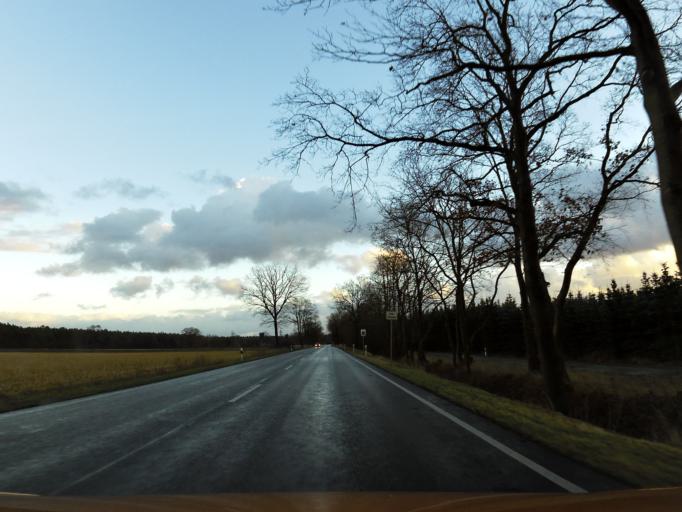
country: DE
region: Lower Saxony
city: Meinersen
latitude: 52.4580
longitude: 10.3008
